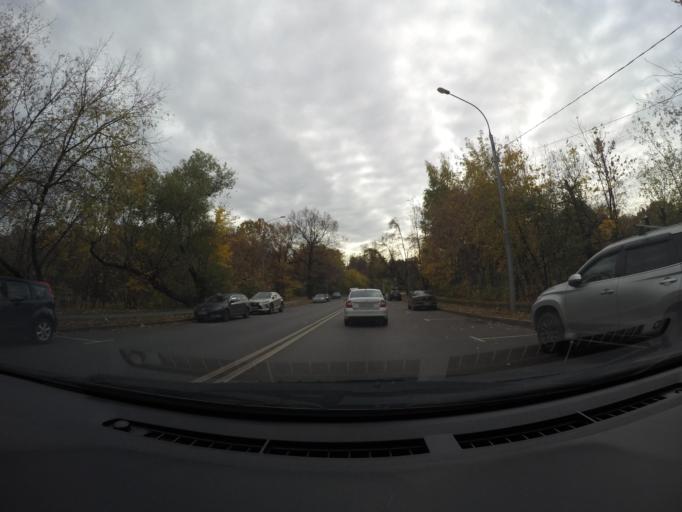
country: RU
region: Moscow
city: Sokol'niki
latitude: 55.8017
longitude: 37.6860
